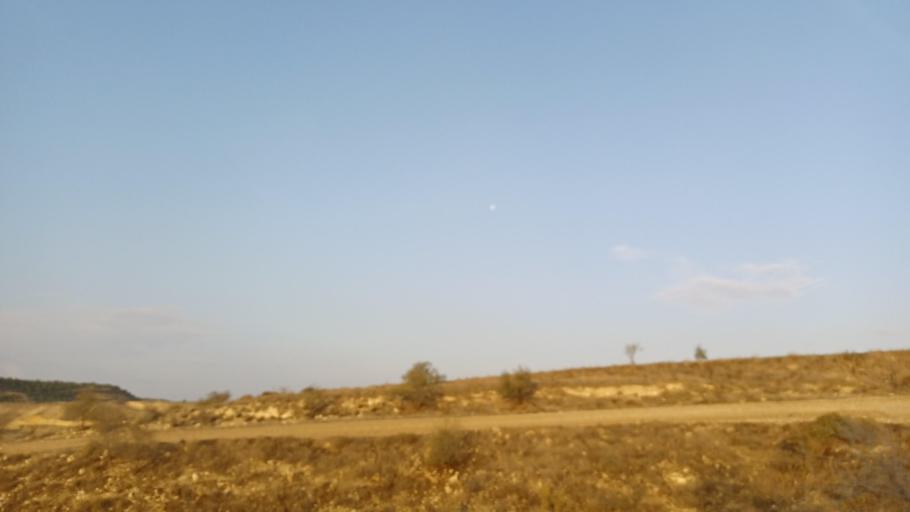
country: CY
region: Larnaka
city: Athienou
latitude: 35.0159
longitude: 33.5321
